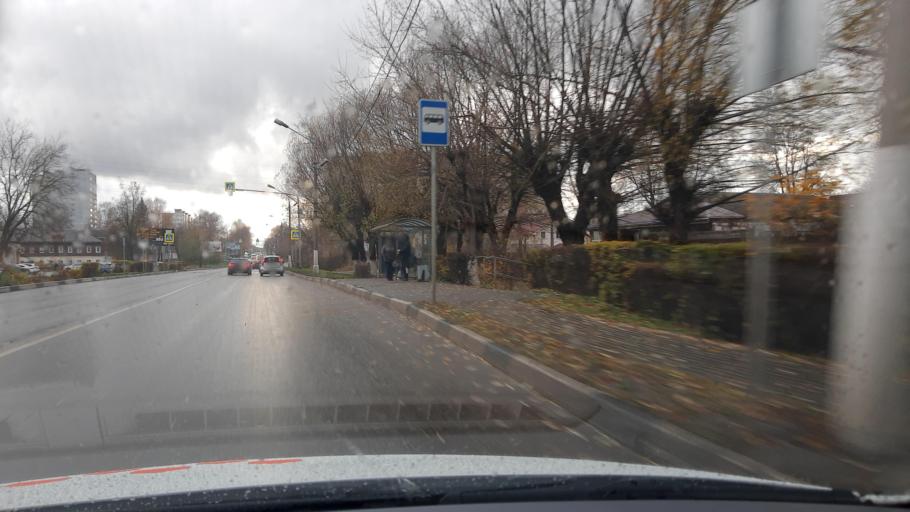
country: RU
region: Moskovskaya
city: Noginsk
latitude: 55.8458
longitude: 38.4128
